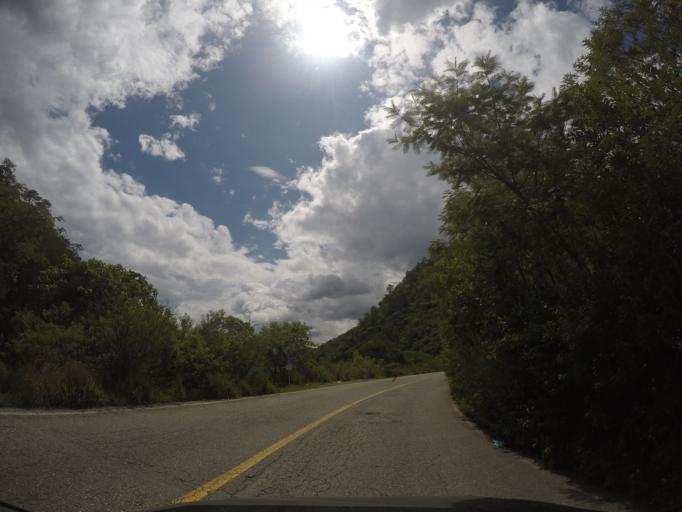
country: MX
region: Oaxaca
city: San Francisco Sola
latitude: 16.4318
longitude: -97.0384
